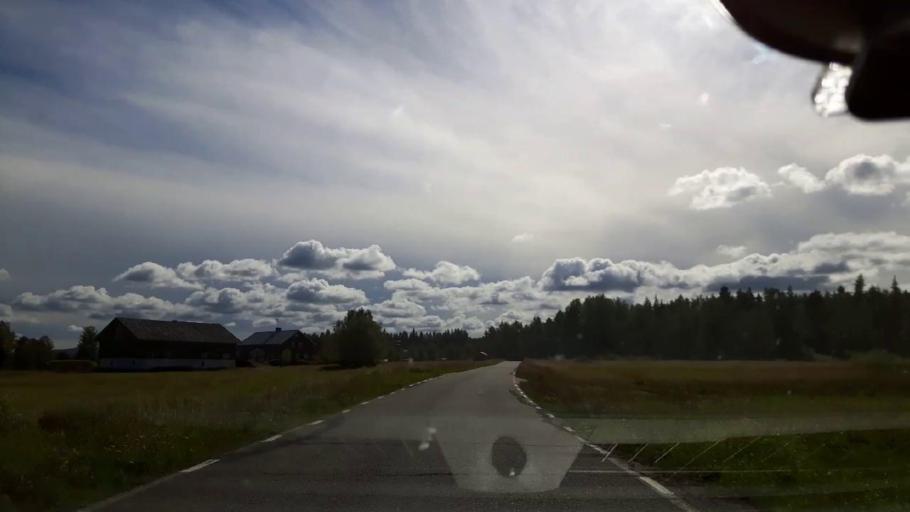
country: SE
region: Jaemtland
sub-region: Braecke Kommun
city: Braecke
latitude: 63.2094
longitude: 15.3505
